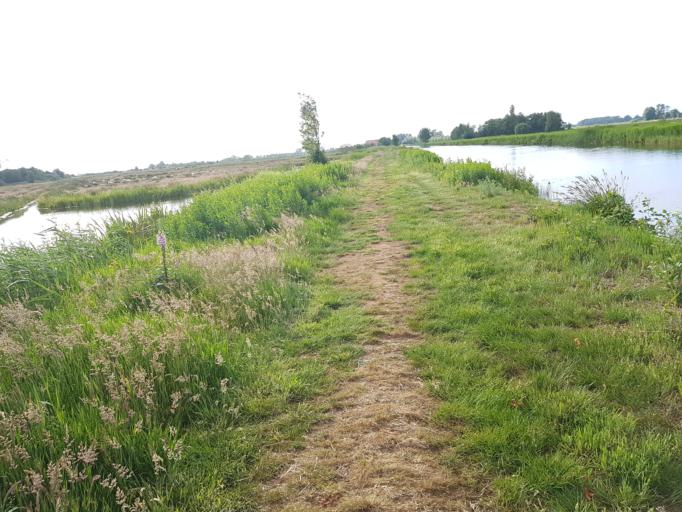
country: NL
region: Friesland
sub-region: Gemeente Smallingerland
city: Oudega
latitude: 53.0897
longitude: 5.9676
